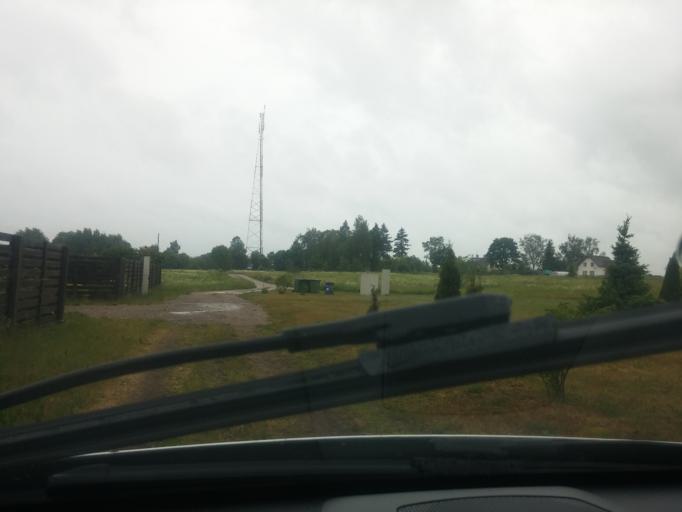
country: LV
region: Ogre
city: Ogre
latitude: 56.8634
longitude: 24.5825
